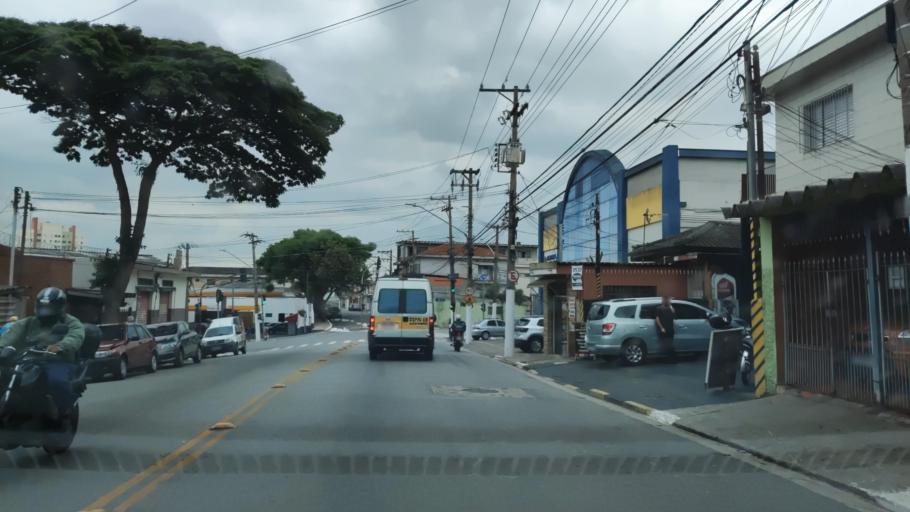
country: BR
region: Sao Paulo
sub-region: Sao Paulo
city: Sao Paulo
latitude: -23.4785
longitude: -46.6508
